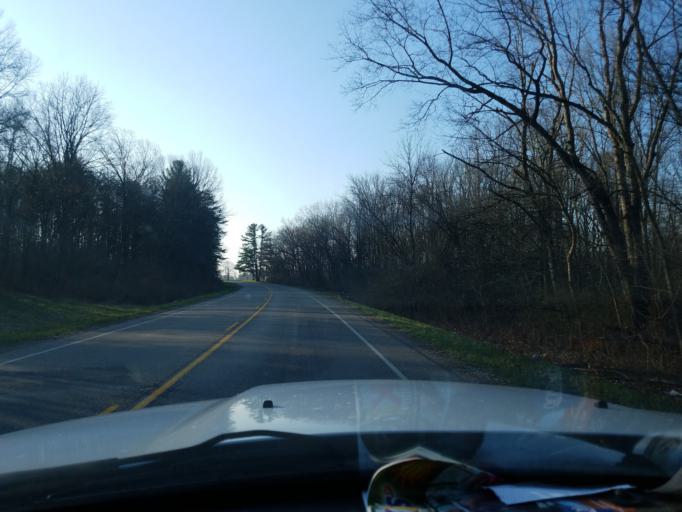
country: US
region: Indiana
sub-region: Vigo County
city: Seelyville
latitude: 39.3997
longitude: -87.3180
